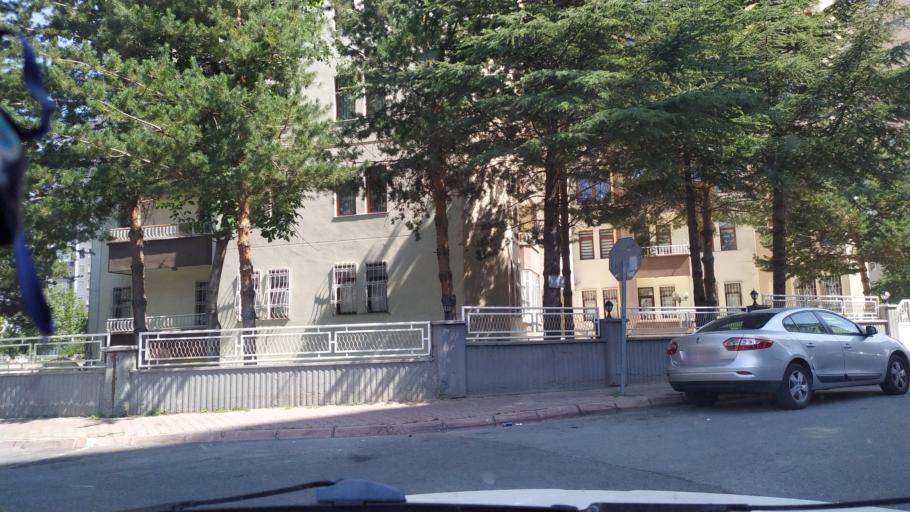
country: TR
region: Kayseri
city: Kayseri
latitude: 38.7288
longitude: 35.5220
